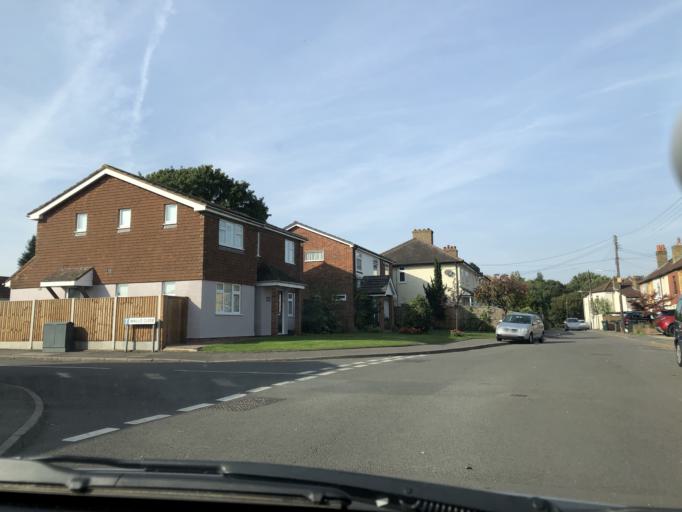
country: GB
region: England
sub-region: Kent
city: Dartford
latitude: 51.4308
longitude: 0.1864
